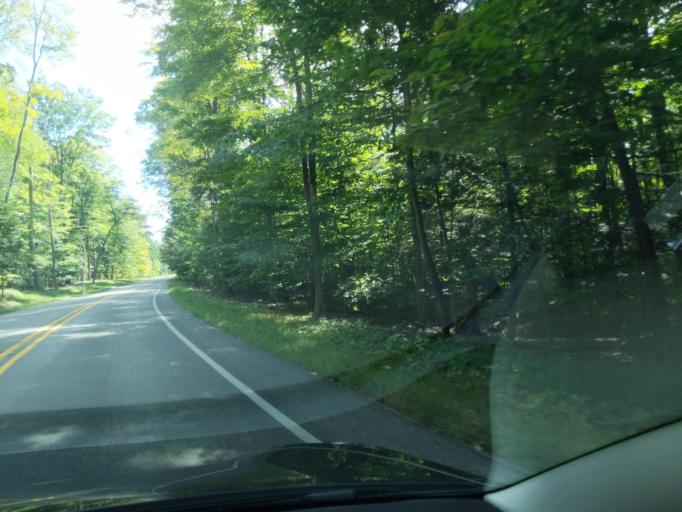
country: US
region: Michigan
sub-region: Antrim County
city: Bellaire
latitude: 45.0230
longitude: -85.2929
